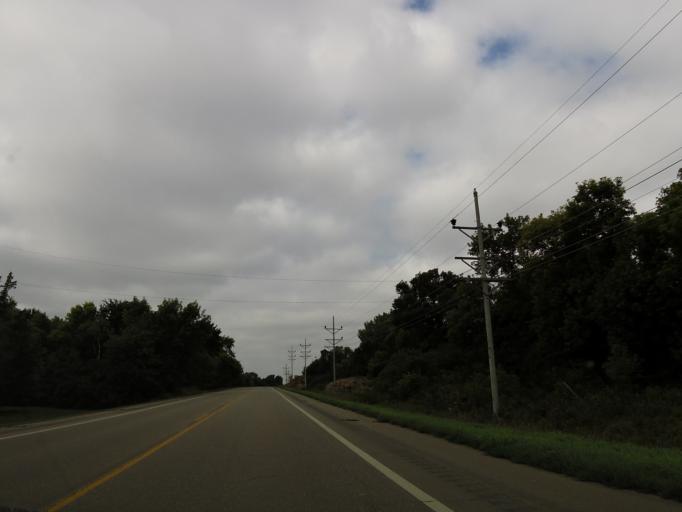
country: US
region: Minnesota
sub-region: Chippewa County
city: Montevideo
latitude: 44.9212
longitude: -95.7006
